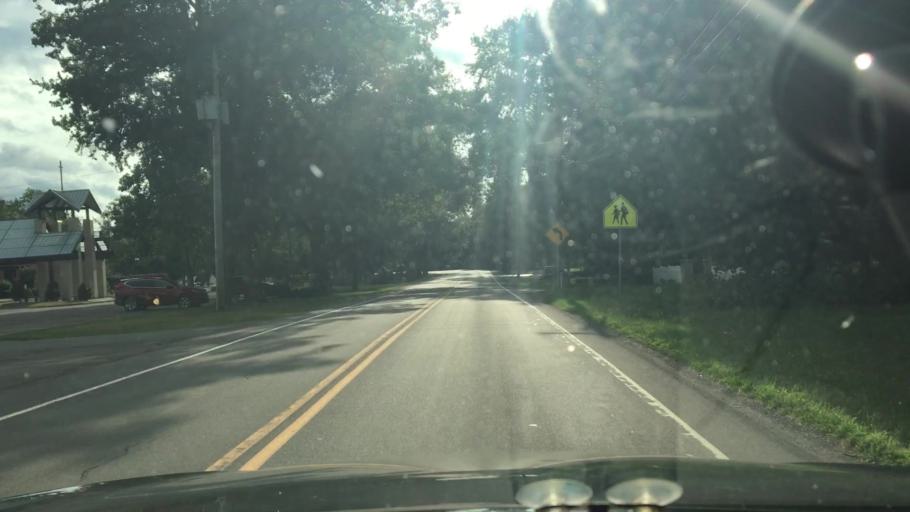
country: US
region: New York
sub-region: Erie County
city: Elma Center
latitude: 42.8179
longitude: -78.6702
